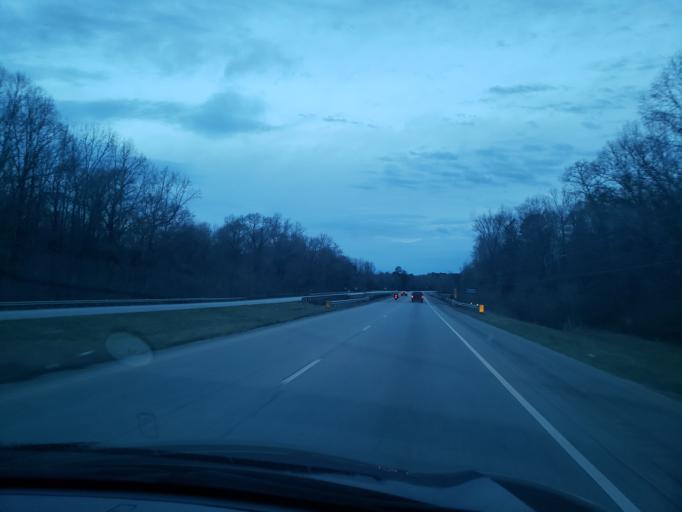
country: US
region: Alabama
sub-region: Lee County
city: Auburn
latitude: 32.6575
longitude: -85.4582
